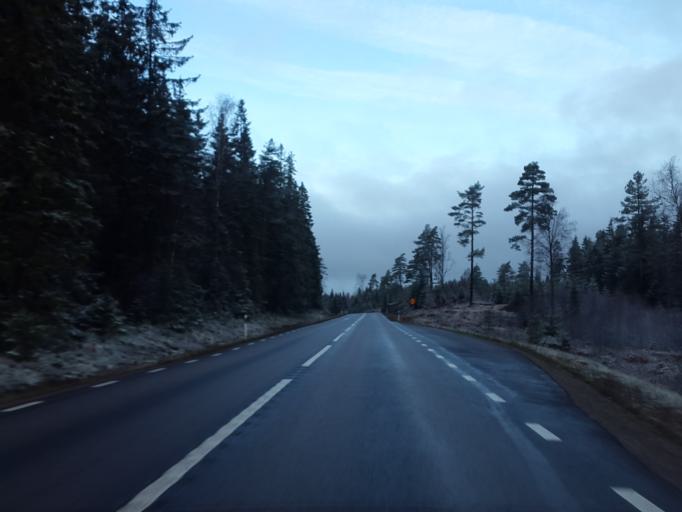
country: SE
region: Vaestra Goetaland
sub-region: Vargarda Kommun
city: Jonstorp
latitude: 57.8384
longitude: 12.6893
